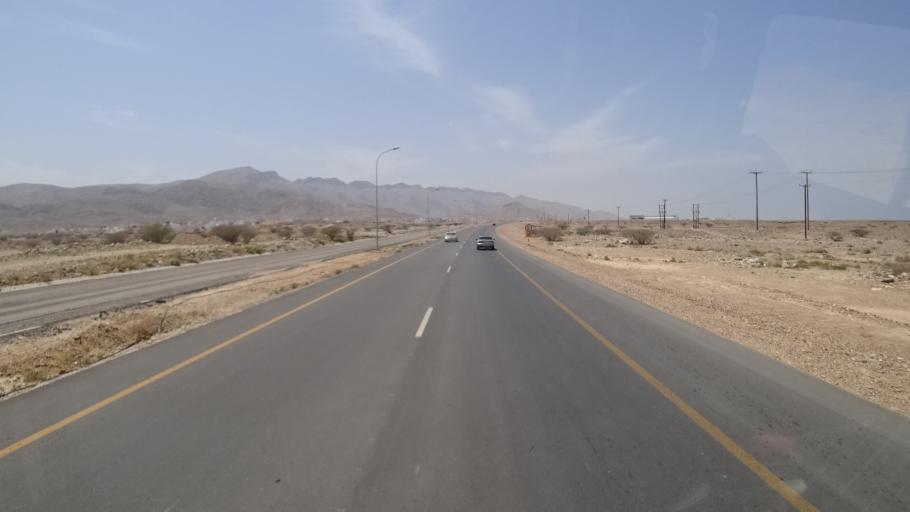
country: OM
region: Ash Sharqiyah
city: Sur
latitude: 22.5852
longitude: 59.4450
